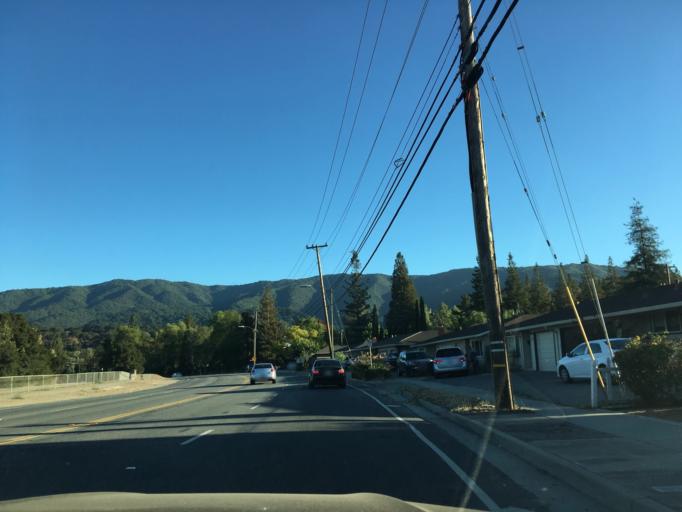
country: US
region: California
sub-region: Santa Clara County
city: Cambrian Park
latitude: 37.2303
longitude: -121.9043
